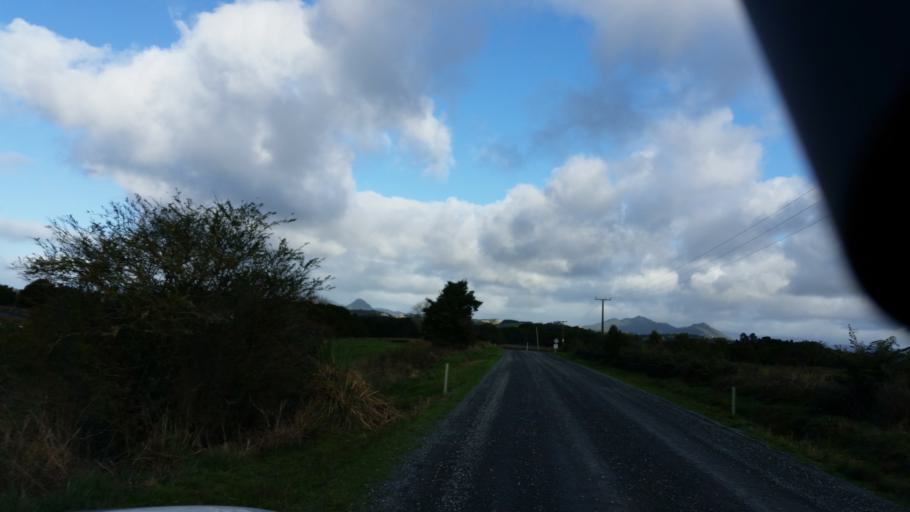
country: NZ
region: Northland
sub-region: Whangarei
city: Maungatapere
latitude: -35.7189
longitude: 174.0714
